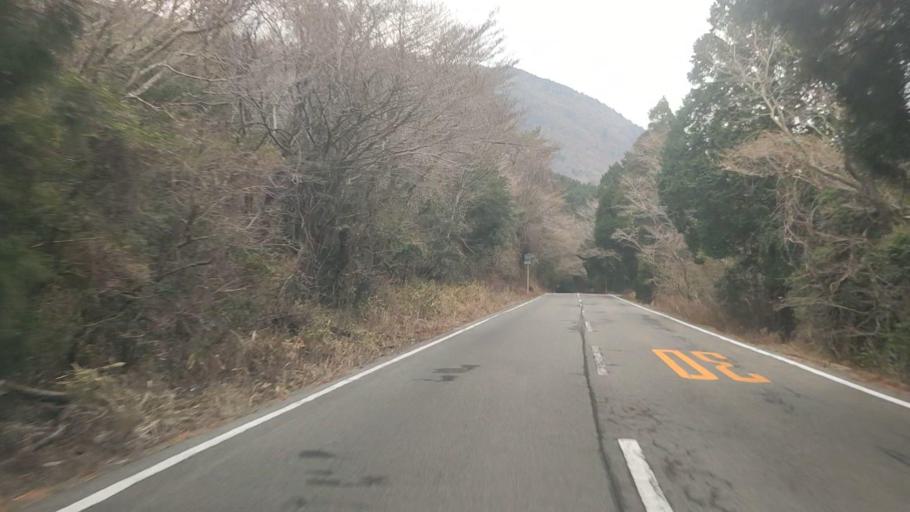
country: JP
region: Nagasaki
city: Shimabara
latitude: 32.7529
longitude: 130.2746
